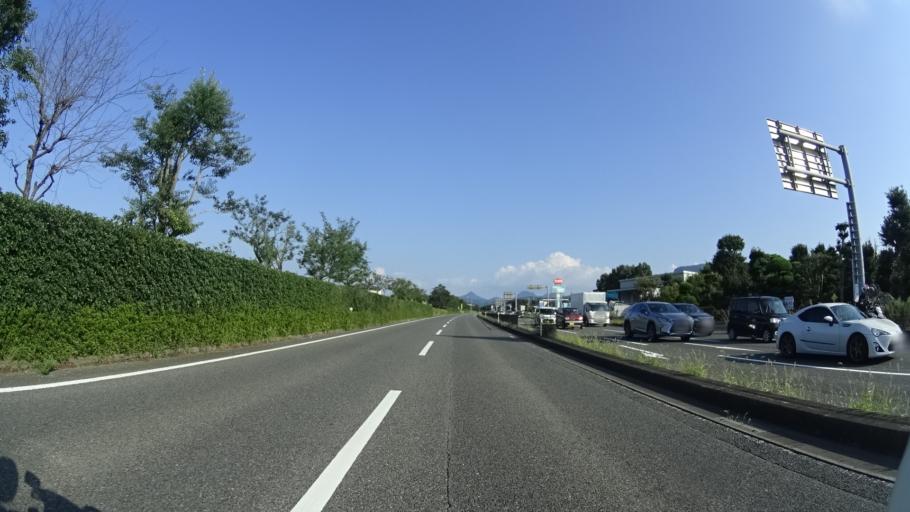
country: JP
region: Fukuoka
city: Nakatsu
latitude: 33.5573
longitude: 131.2025
